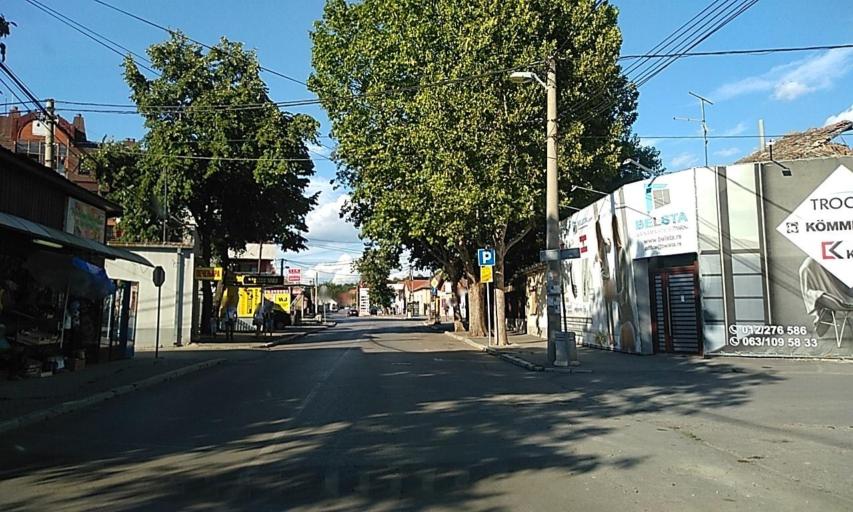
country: RS
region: Central Serbia
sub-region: Branicevski Okrug
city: Pozarevac
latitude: 44.6248
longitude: 21.1891
